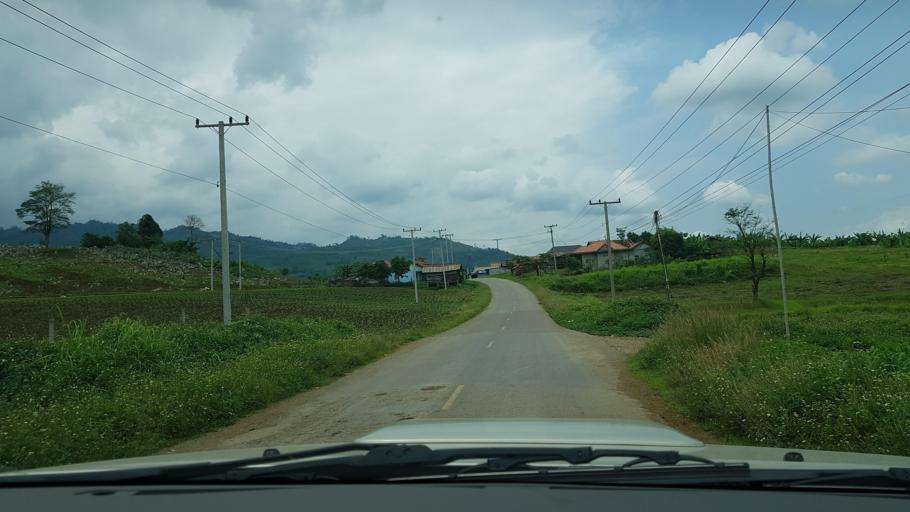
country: TH
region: Nan
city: Chaloem Phra Kiat
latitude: 19.9833
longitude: 101.2749
